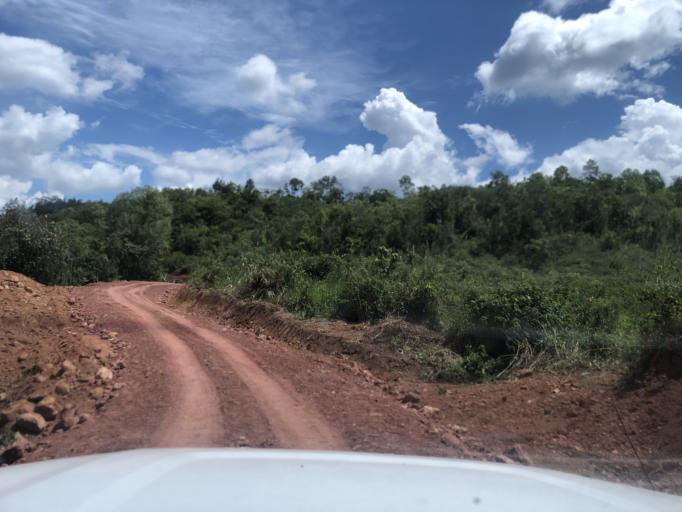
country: CN
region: Yunnan
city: Menglie
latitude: 22.2326
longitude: 101.6198
